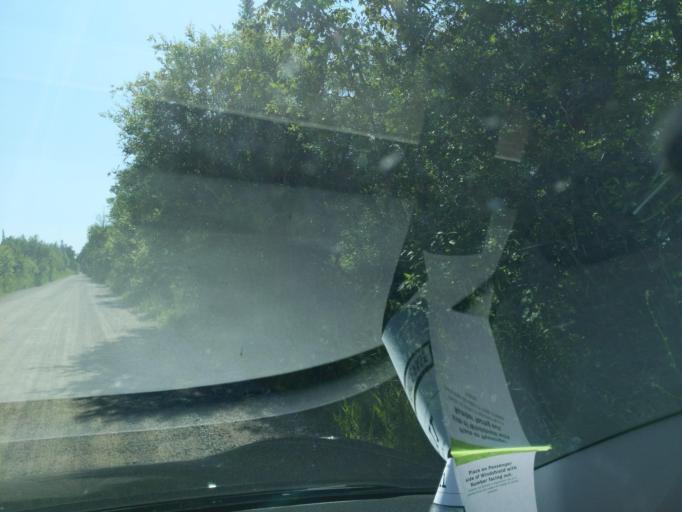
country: US
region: Michigan
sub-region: Mackinac County
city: Saint Ignace
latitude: 45.6795
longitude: -84.6991
